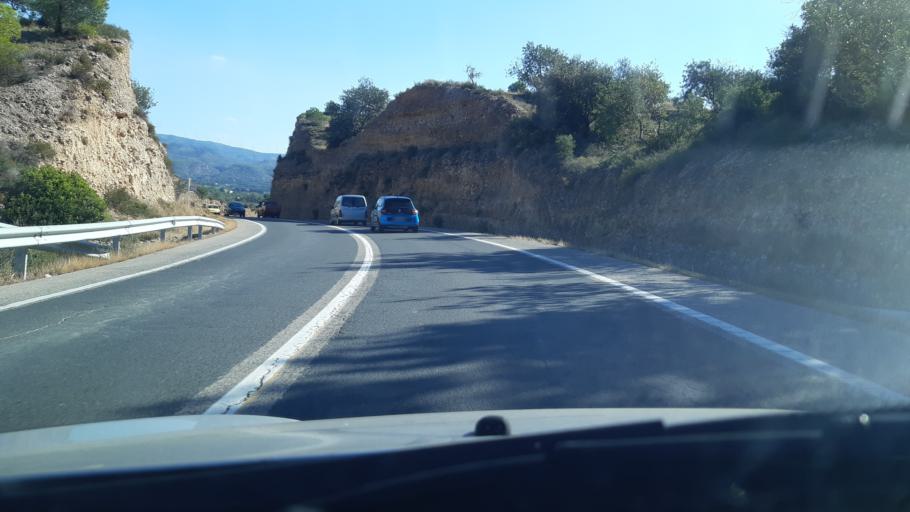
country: ES
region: Catalonia
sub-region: Provincia de Tarragona
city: Tivenys
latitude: 40.8789
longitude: 0.4978
